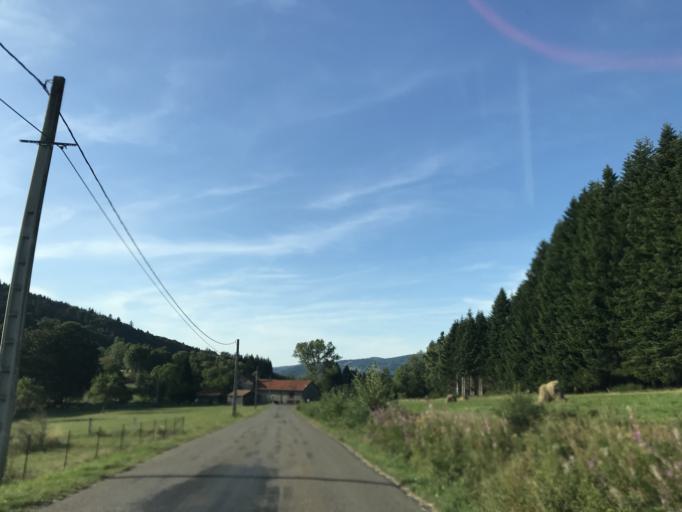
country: FR
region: Auvergne
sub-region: Departement du Puy-de-Dome
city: Job
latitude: 45.6794
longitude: 3.7294
